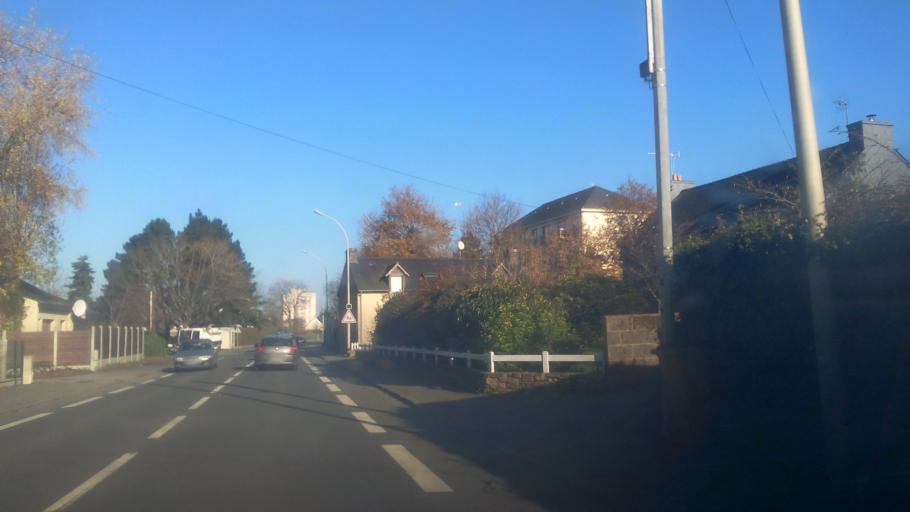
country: FR
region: Brittany
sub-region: Departement d'Ille-et-Vilaine
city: Redon
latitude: 47.6605
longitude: -2.0718
